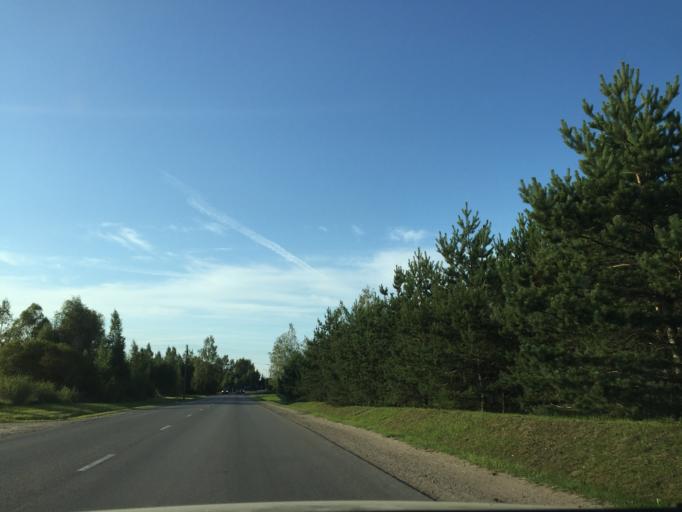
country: LT
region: Panevezys
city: Rokiskis
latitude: 55.9497
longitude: 25.5765
